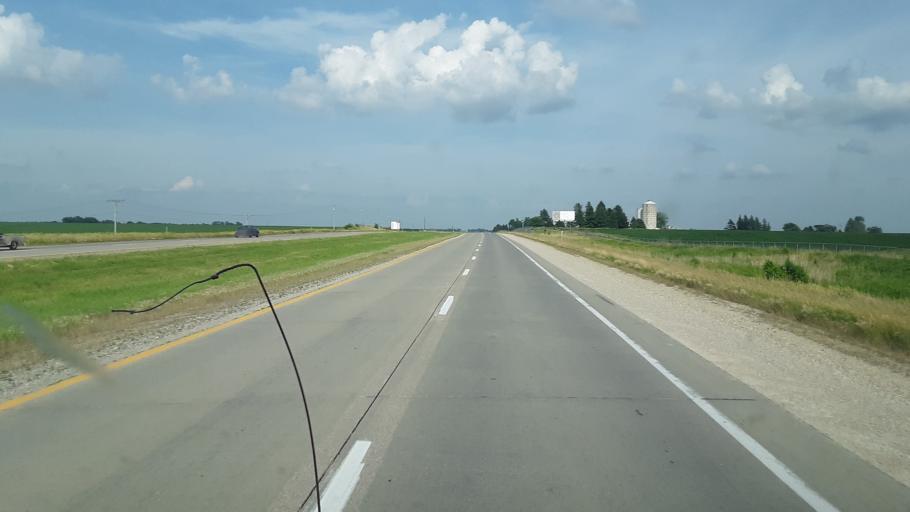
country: US
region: Iowa
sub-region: Marshall County
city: Marshalltown
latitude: 42.0077
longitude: -93.0089
